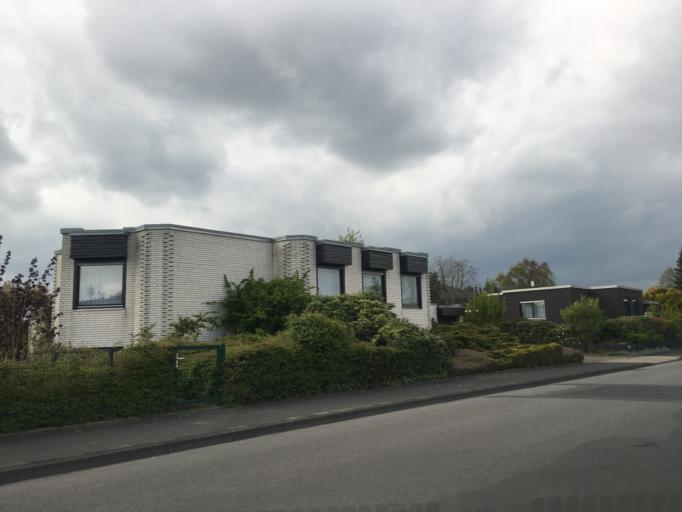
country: DE
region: North Rhine-Westphalia
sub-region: Regierungsbezirk Munster
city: Steinfurt
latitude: 52.1384
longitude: 7.3351
